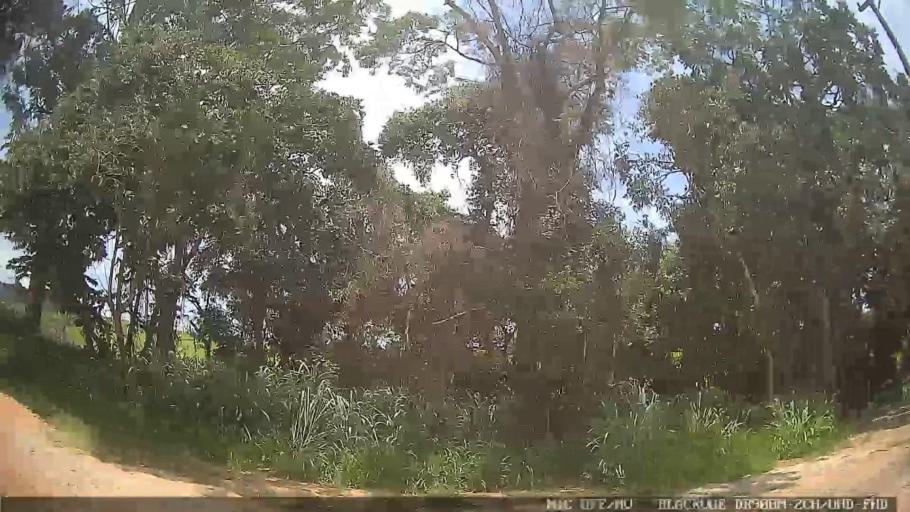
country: BR
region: Sao Paulo
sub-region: Atibaia
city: Atibaia
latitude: -23.0957
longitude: -46.6180
